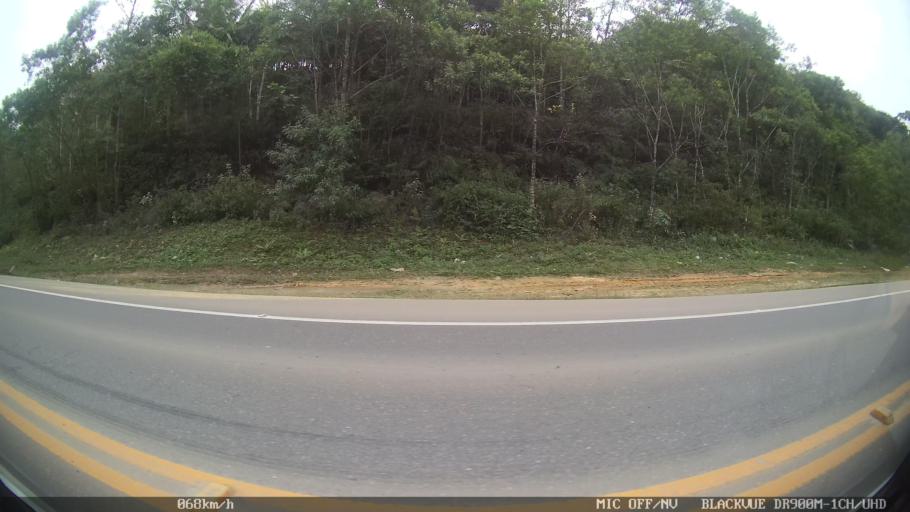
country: BR
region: Santa Catarina
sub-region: Joinville
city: Joinville
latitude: -26.2637
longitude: -48.9172
